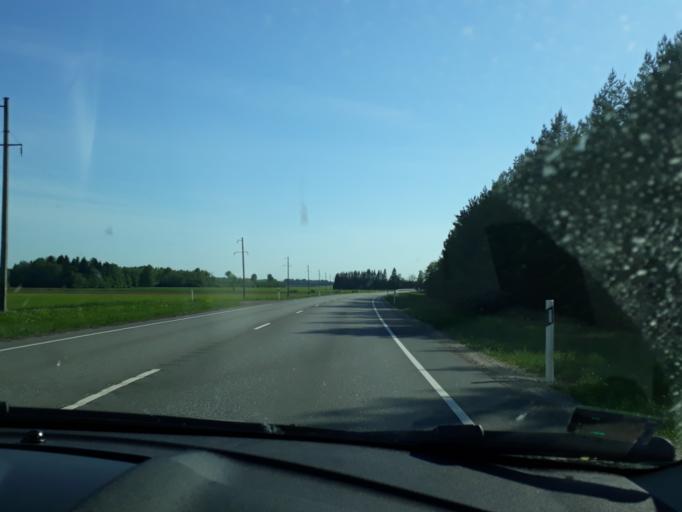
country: EE
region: Paernumaa
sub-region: Tootsi vald
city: Tootsi
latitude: 58.5622
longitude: 24.8695
